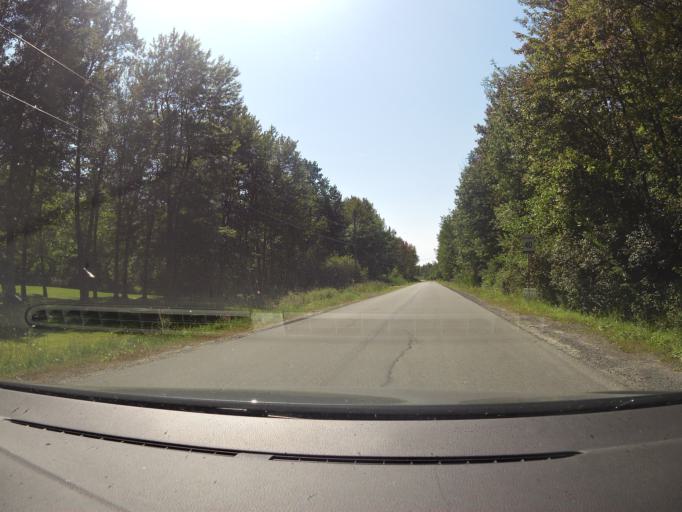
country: CA
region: Ontario
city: Bells Corners
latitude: 45.2869
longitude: -75.9901
